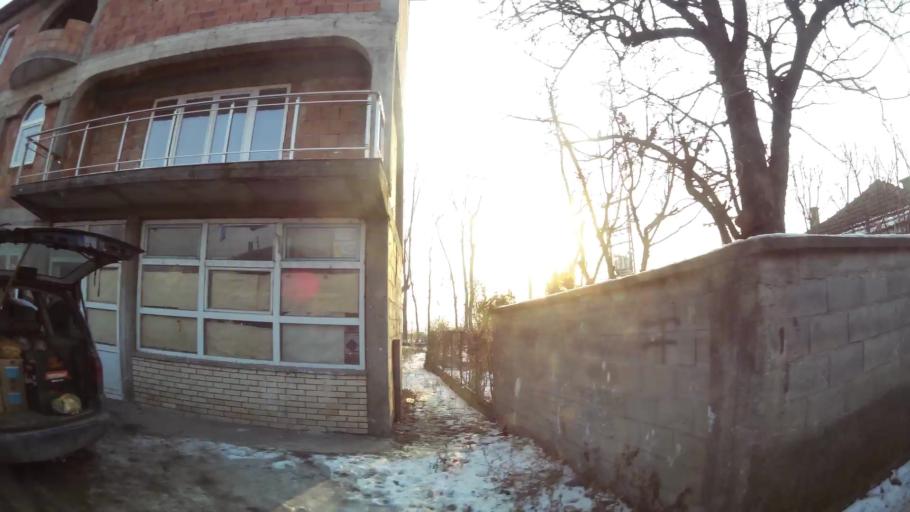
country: MK
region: Aracinovo
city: Arachinovo
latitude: 42.0136
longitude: 21.5262
